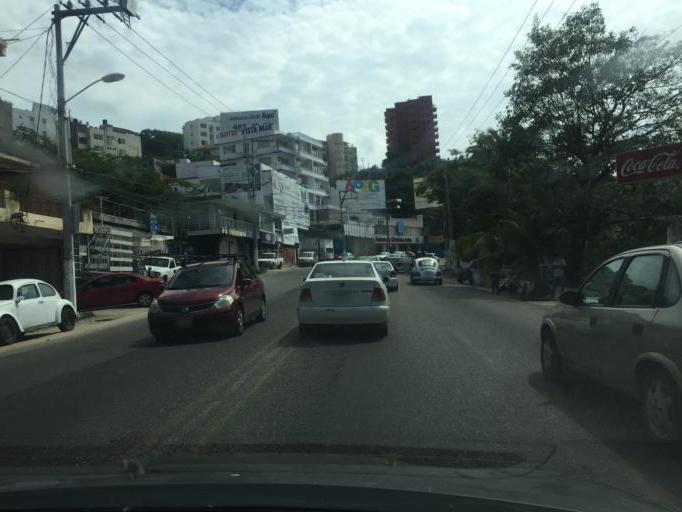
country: MX
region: Guerrero
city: Acapulco de Juarez
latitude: 16.8630
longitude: -99.8692
